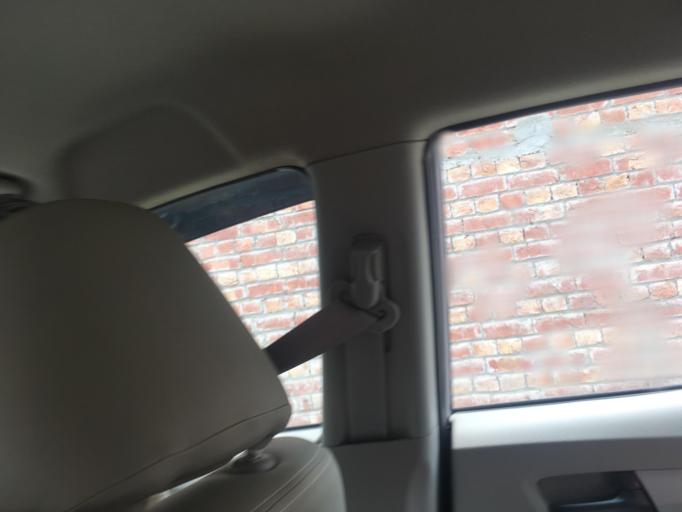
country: PK
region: Punjab
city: Lahore
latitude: 31.6122
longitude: 74.3542
